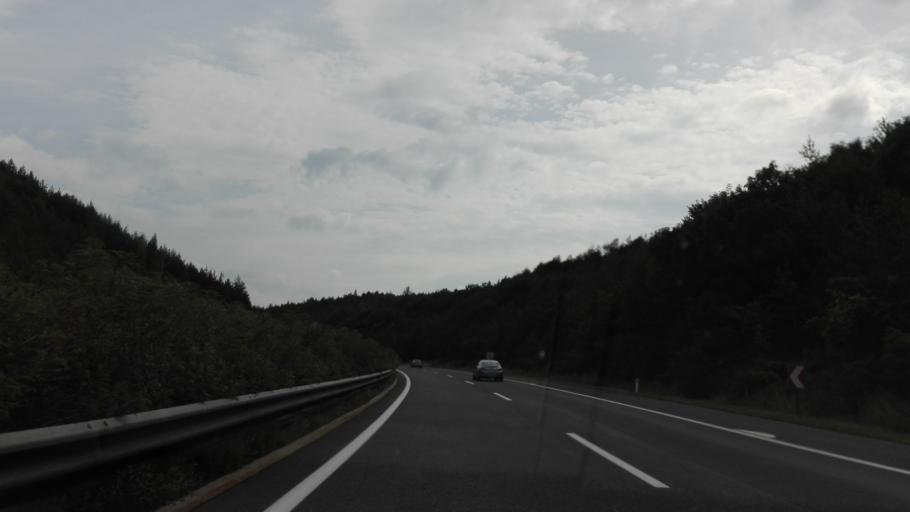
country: AT
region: Lower Austria
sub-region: Politischer Bezirk Baden
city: Heiligenkreuz
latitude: 48.0566
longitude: 16.1068
